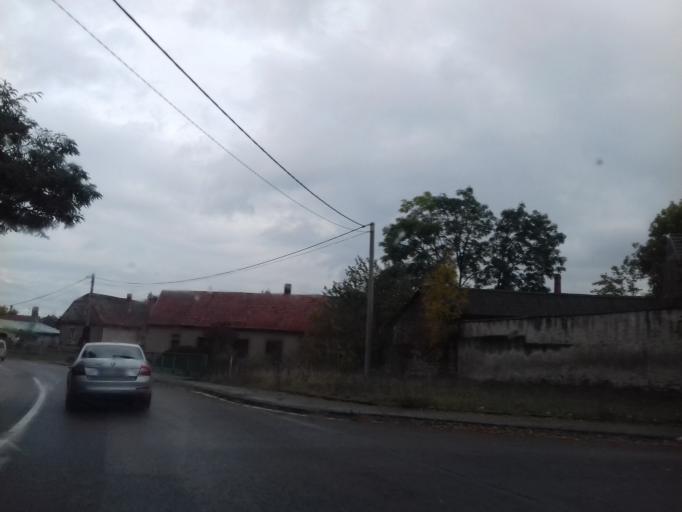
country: CZ
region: Pardubicky
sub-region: Okres Chrudim
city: Chrast
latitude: 49.8949
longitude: 15.9538
